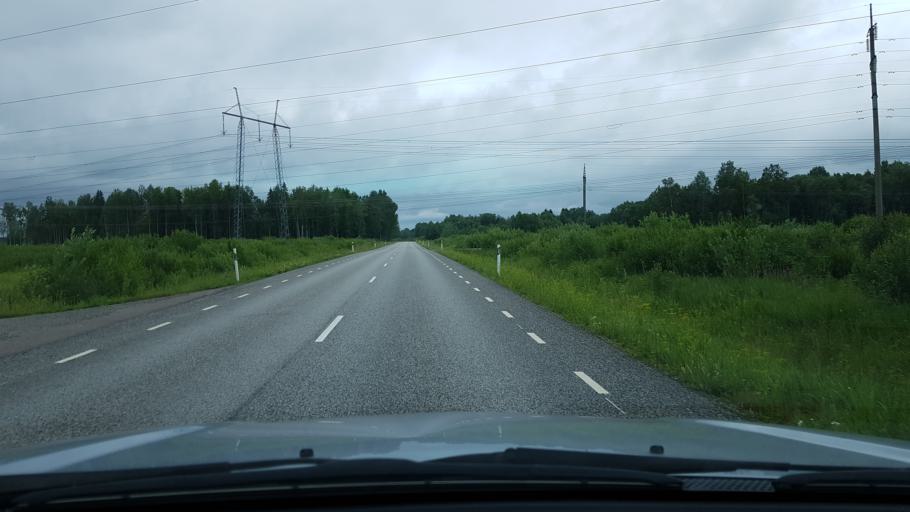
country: EE
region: Ida-Virumaa
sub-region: Narva-Joesuu linn
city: Narva-Joesuu
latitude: 59.3514
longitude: 27.9299
